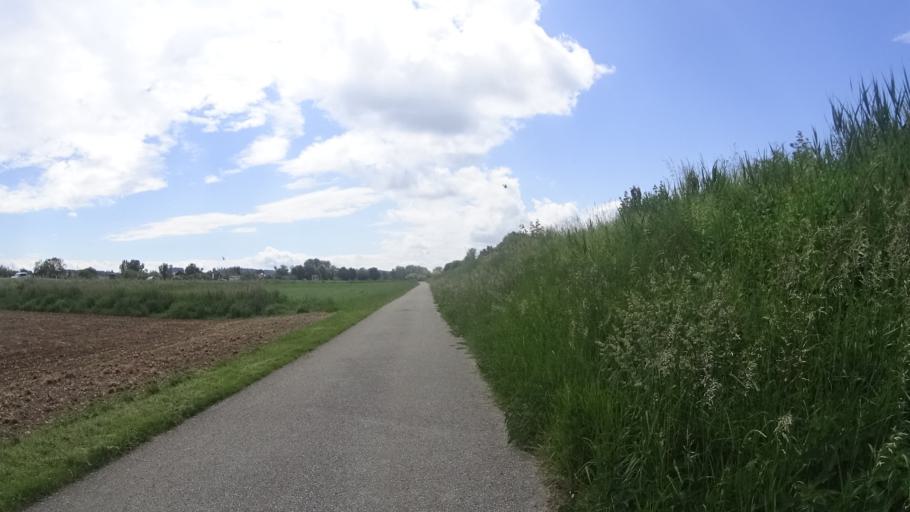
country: DE
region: Bavaria
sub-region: Lower Bavaria
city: Unterdietfurt
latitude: 48.3967
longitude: 12.7058
